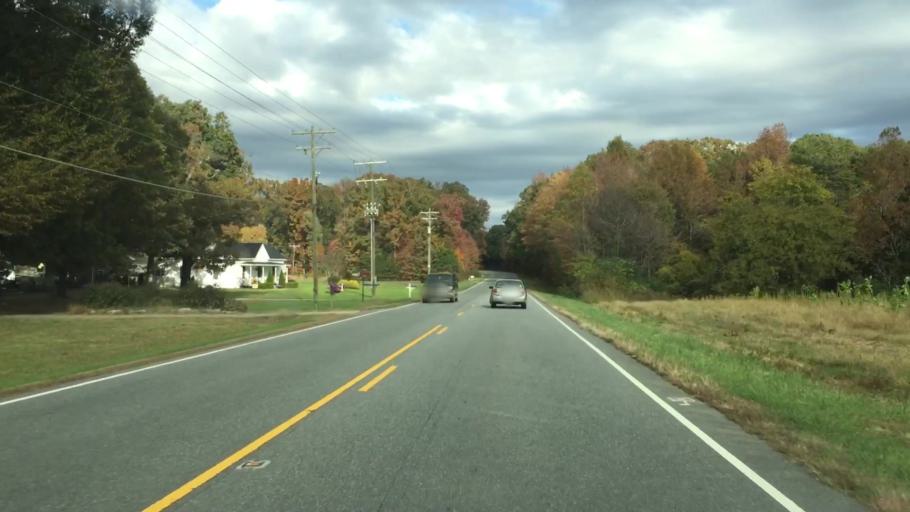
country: US
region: North Carolina
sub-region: Rockingham County
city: Wentworth
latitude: 36.2788
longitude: -79.7629
